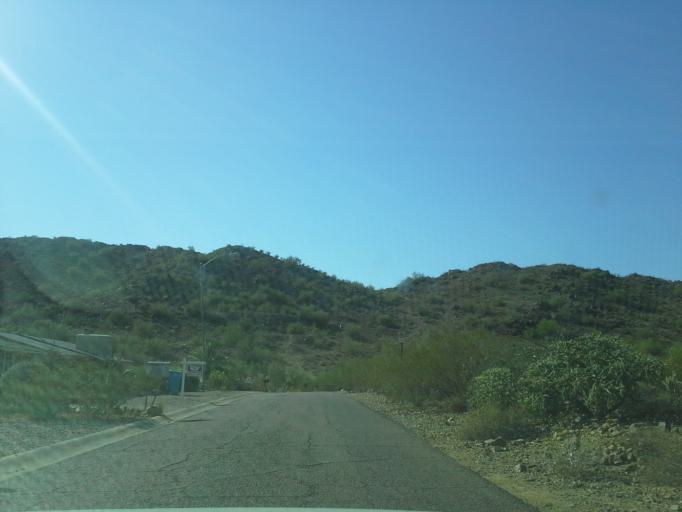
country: US
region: Arizona
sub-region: Maricopa County
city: Glendale
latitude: 33.5857
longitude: -112.0839
